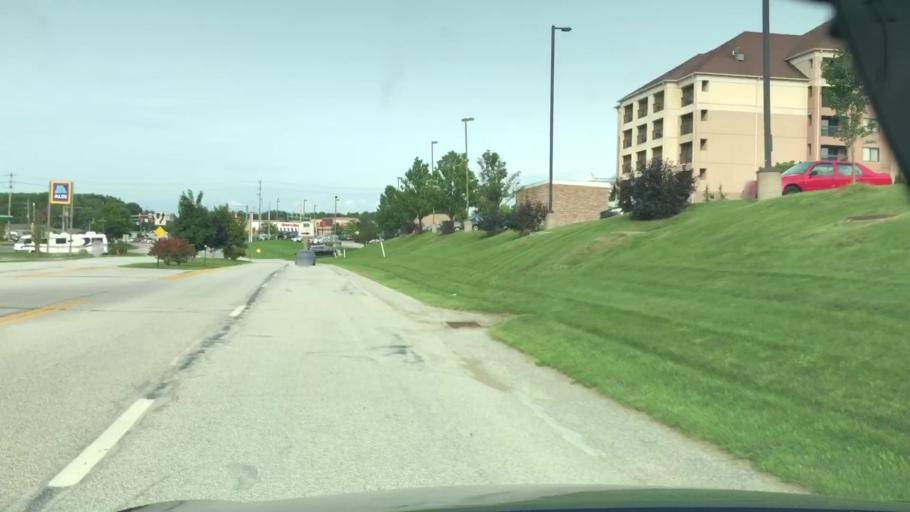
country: US
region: Pennsylvania
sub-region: Erie County
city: Erie
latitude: 42.0503
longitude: -80.0858
